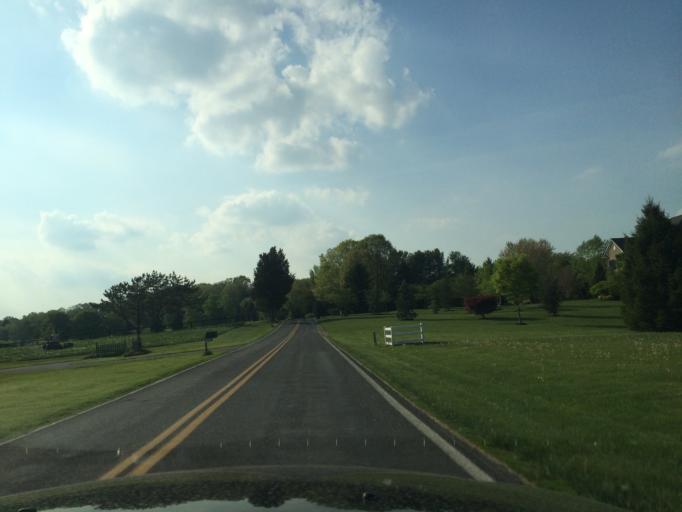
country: US
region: Maryland
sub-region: Carroll County
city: Mount Airy
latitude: 39.2955
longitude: -77.0829
